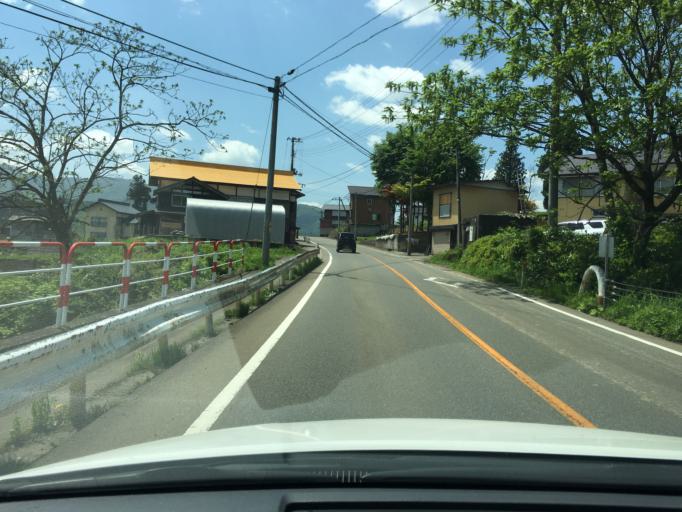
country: JP
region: Niigata
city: Tochio-honcho
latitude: 37.3309
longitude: 139.0270
